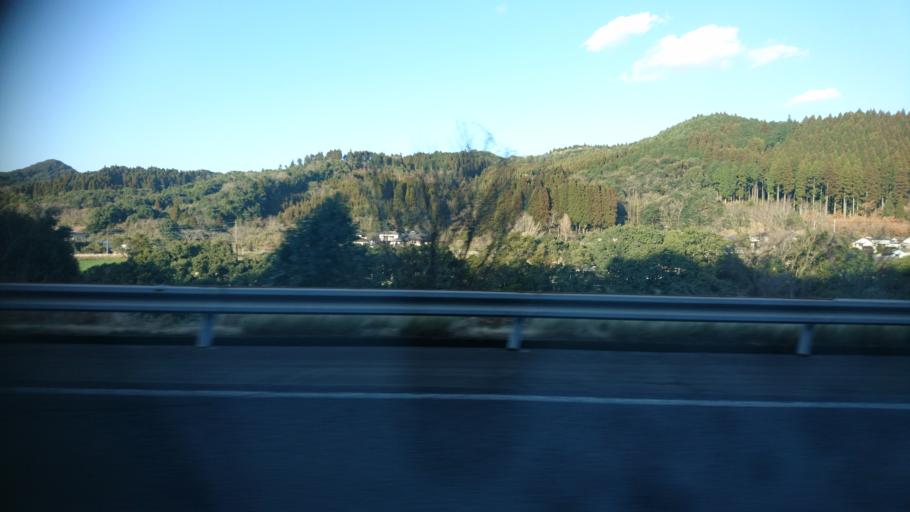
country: JP
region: Miyazaki
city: Miyakonojo
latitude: 31.7927
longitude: 131.1781
